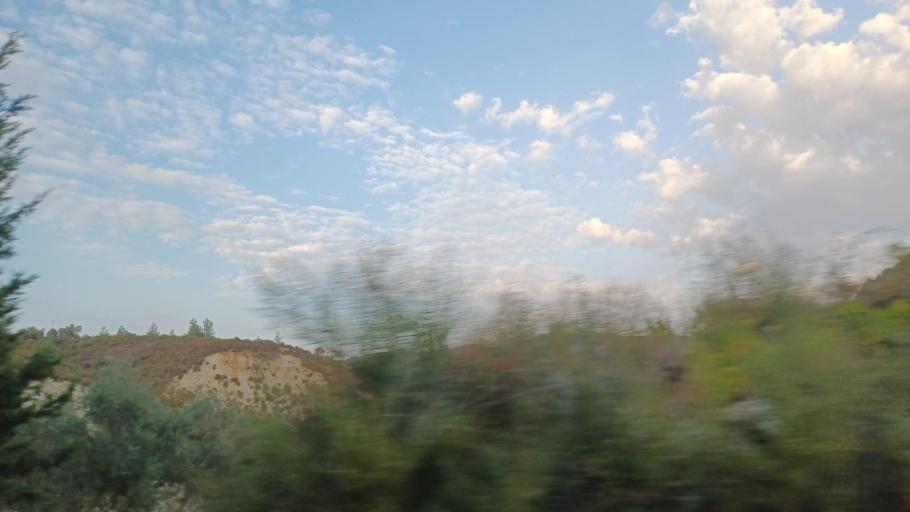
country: CY
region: Limassol
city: Pelendri
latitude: 34.8127
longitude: 32.9592
